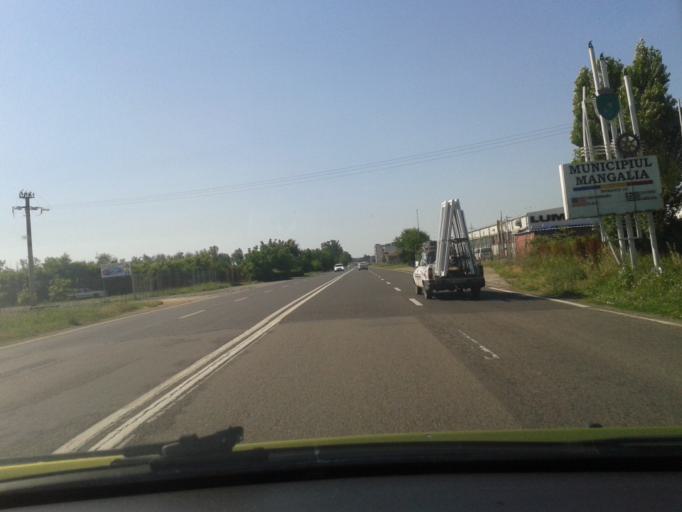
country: RO
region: Constanta
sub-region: Municipiul Mangalia
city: Mangalia
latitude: 43.8363
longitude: 28.5768
